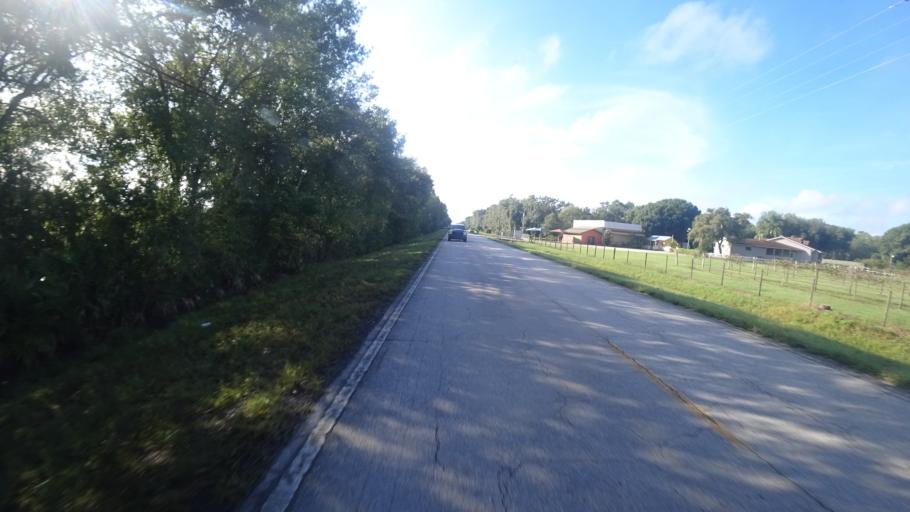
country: US
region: Florida
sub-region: Sarasota County
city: The Meadows
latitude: 27.4628
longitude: -82.3032
